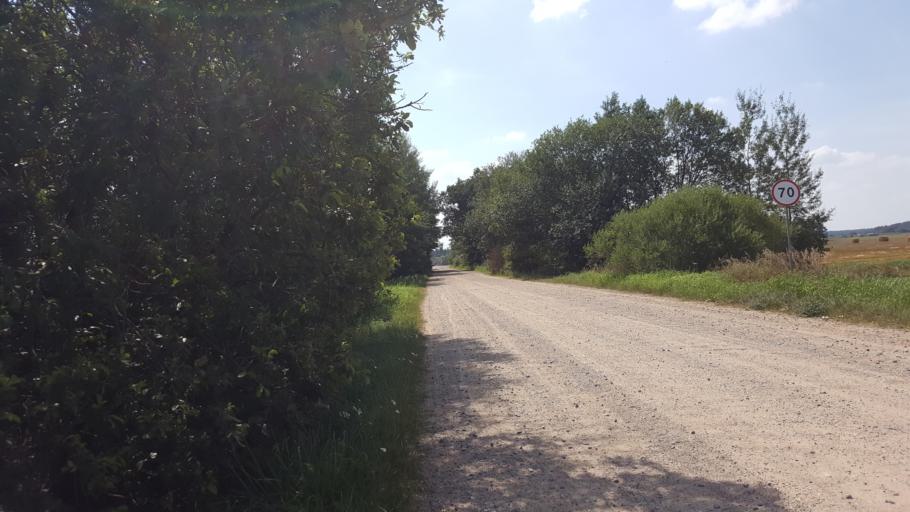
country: PL
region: Podlasie
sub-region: Powiat hajnowski
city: Hajnowka
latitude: 52.5479
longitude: 23.5467
